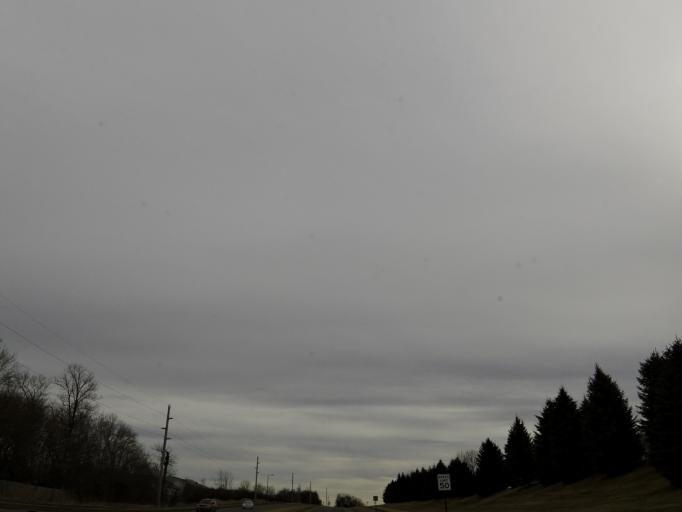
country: US
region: Minnesota
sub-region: Scott County
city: Savage
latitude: 44.7440
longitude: -93.3590
